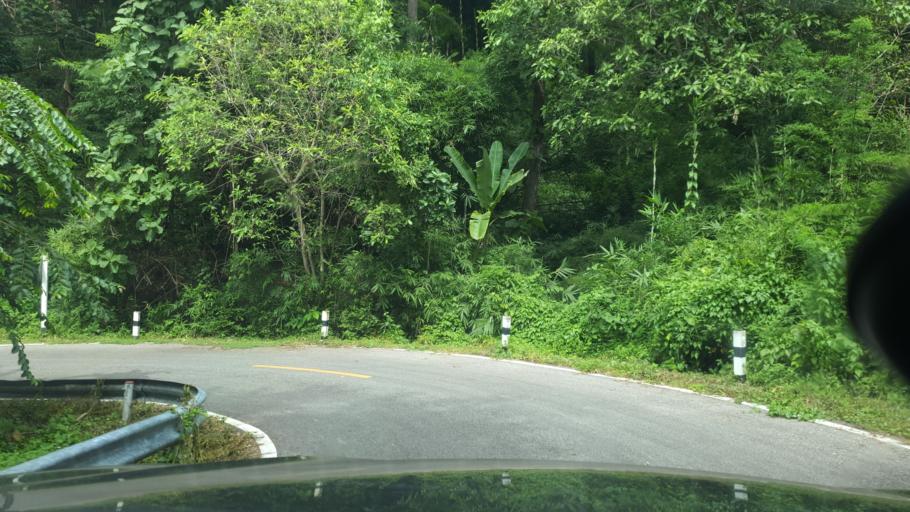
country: TH
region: Lamphun
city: Mae Tha
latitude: 18.4987
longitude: 99.2691
